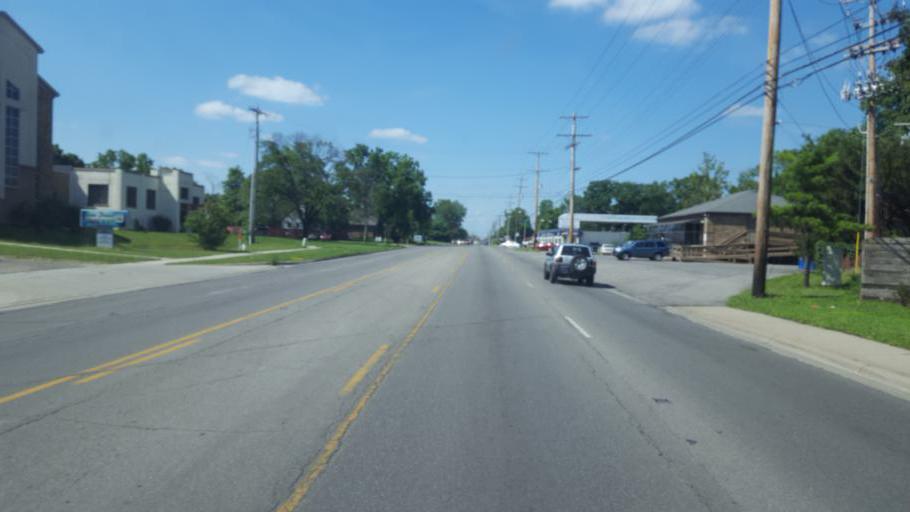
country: US
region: Ohio
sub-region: Franklin County
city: Minerva Park
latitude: 40.0751
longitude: -82.9518
